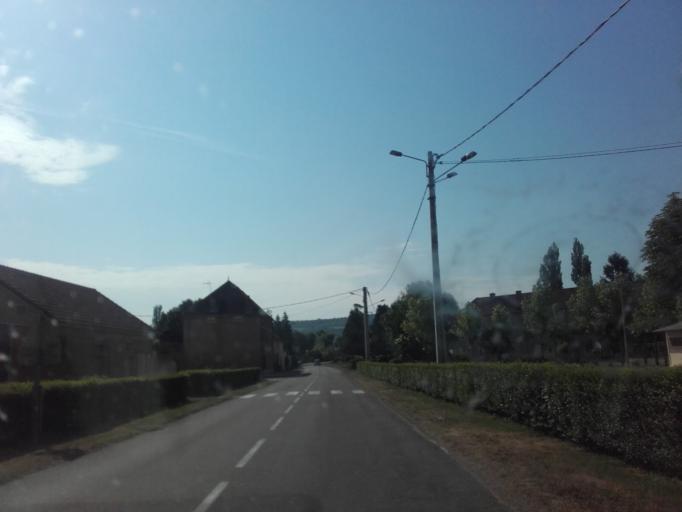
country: FR
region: Bourgogne
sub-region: Departement de Saone-et-Loire
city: Chagny
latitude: 46.9100
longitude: 4.7039
